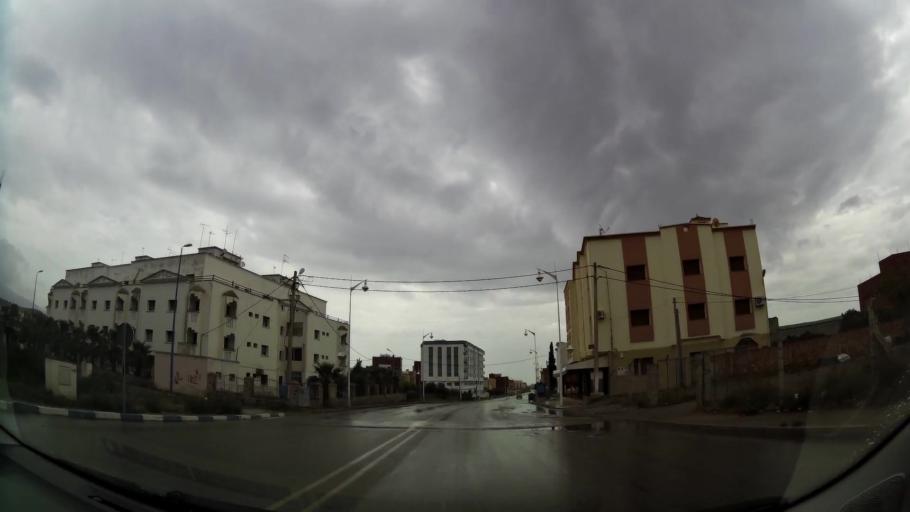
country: MA
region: Oriental
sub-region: Nador
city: Nador
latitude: 35.1522
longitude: -2.9941
